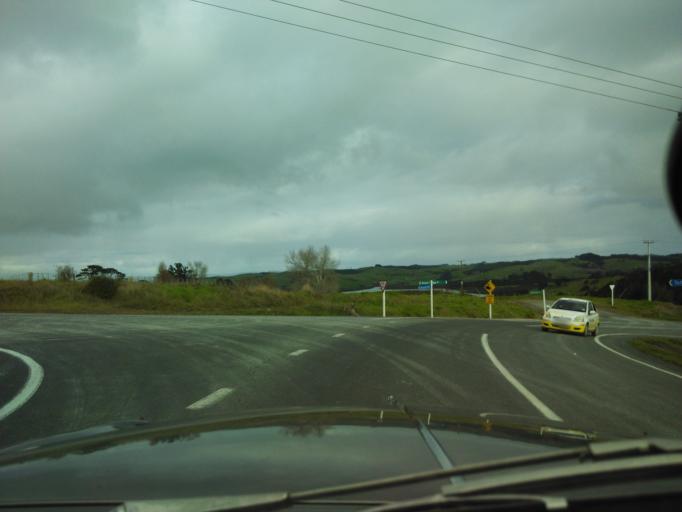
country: NZ
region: Auckland
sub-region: Auckland
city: Wellsford
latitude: -36.3296
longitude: 174.4162
